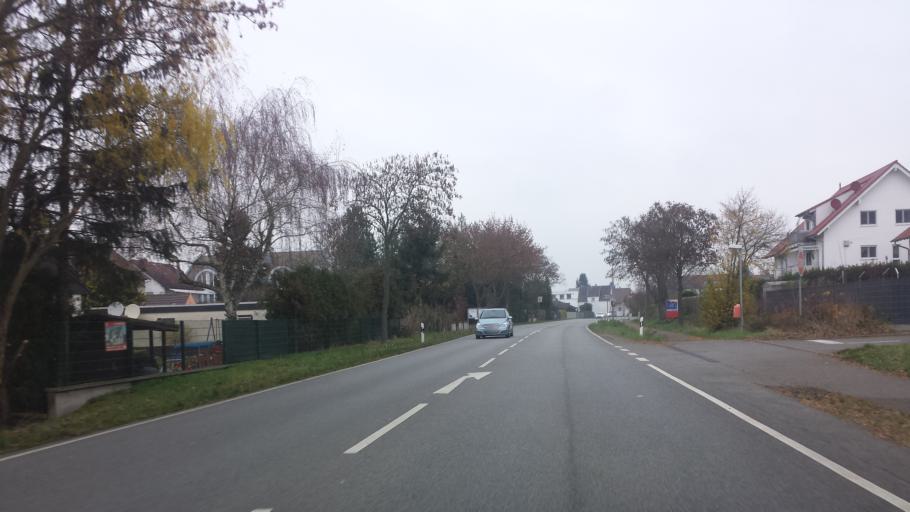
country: DE
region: Hesse
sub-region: Regierungsbezirk Darmstadt
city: Burstadt
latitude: 49.6598
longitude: 8.4498
